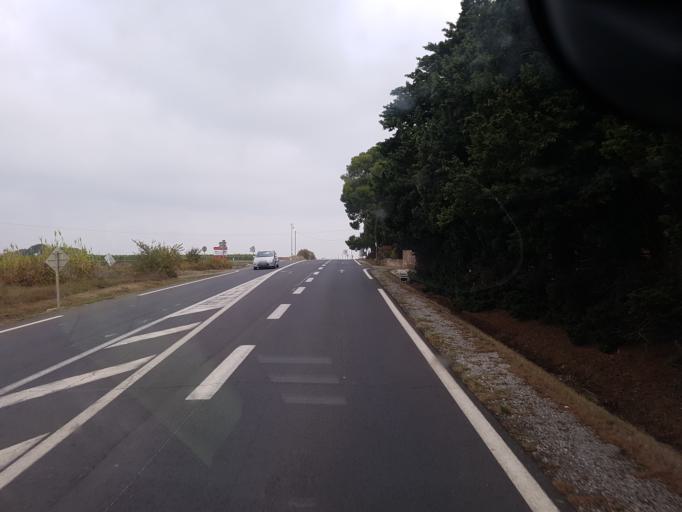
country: FR
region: Languedoc-Roussillon
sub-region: Departement de l'Herault
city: Pinet
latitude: 43.3891
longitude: 3.5374
